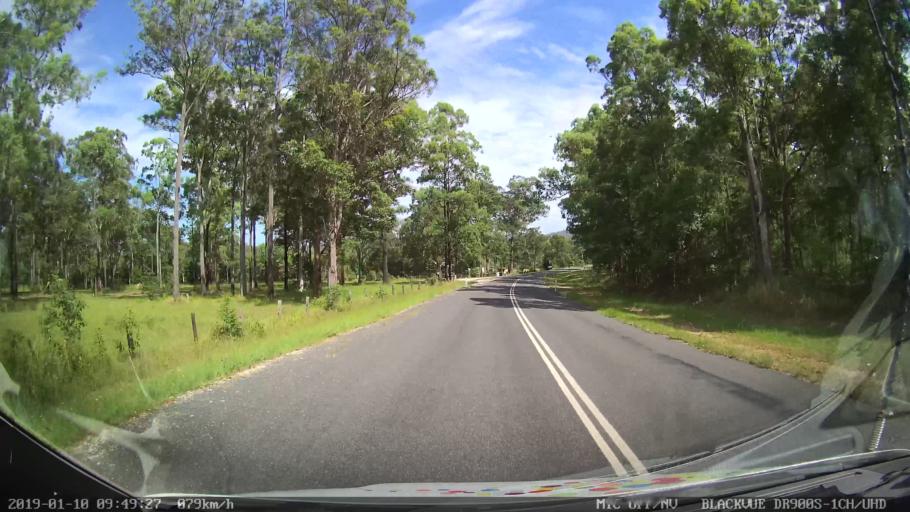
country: AU
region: New South Wales
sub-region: Coffs Harbour
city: Nana Glen
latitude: -30.0628
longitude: 152.9782
